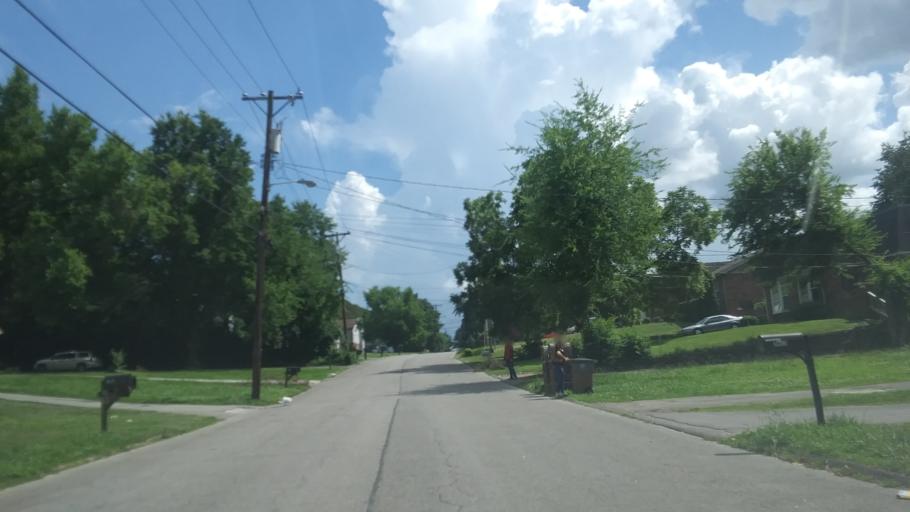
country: US
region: Tennessee
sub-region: Davidson County
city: Oak Hill
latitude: 36.0718
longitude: -86.7102
